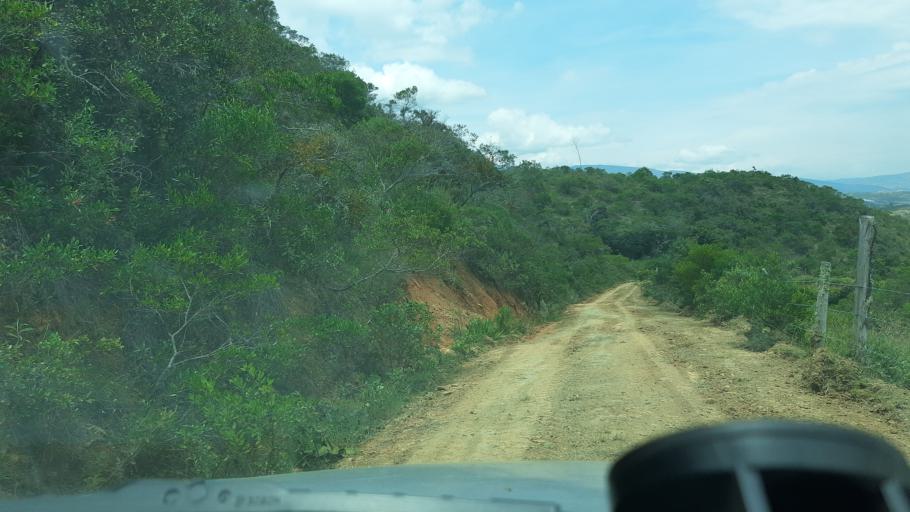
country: CO
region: Boyaca
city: Santa Sofia
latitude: 5.6960
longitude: -73.5802
